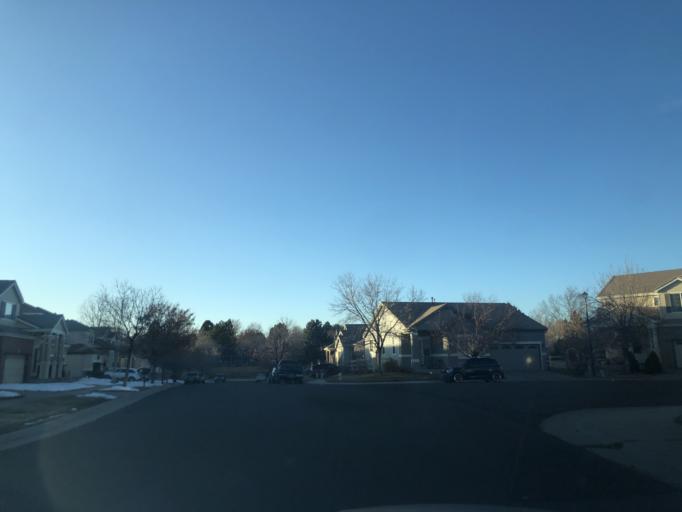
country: US
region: Colorado
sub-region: Adams County
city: Aurora
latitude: 39.7158
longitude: -104.8127
